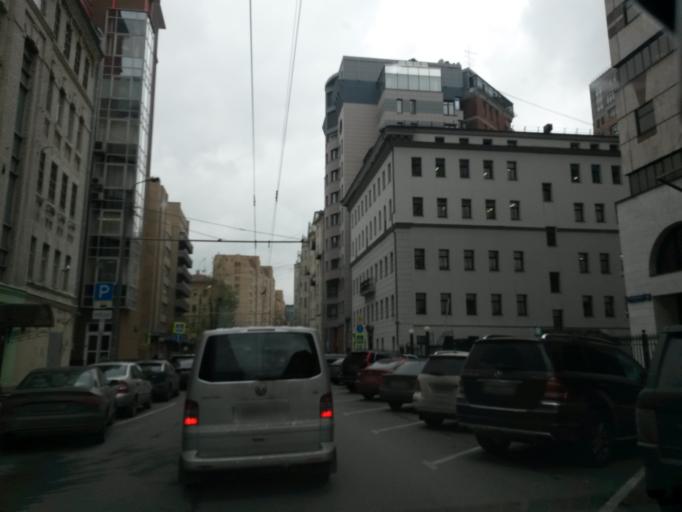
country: RU
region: Moscow
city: Moscow
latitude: 55.7735
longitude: 37.5954
